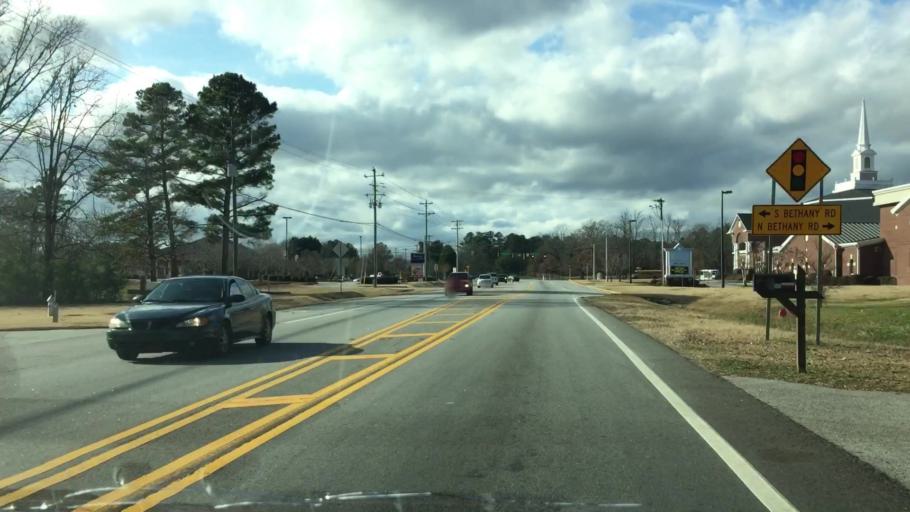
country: US
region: Georgia
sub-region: Henry County
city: McDonough
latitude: 33.4284
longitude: -84.0884
